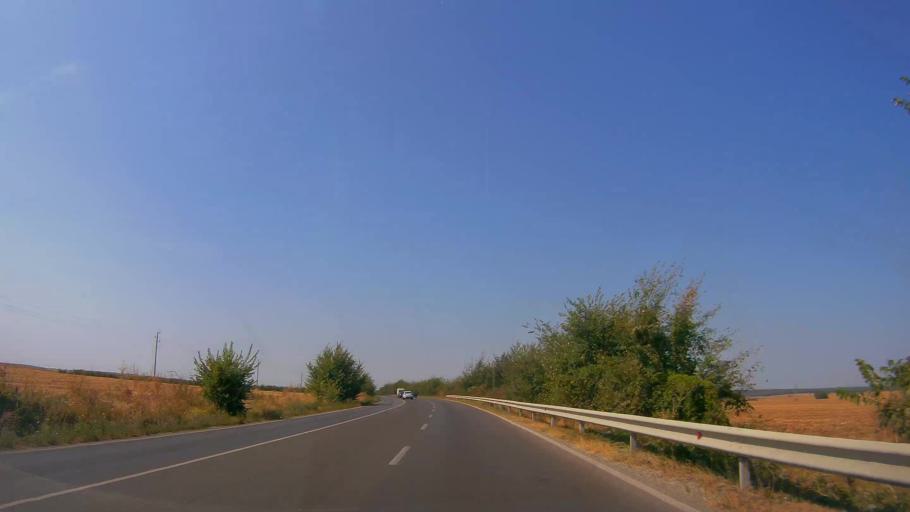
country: BG
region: Ruse
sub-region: Obshtina Vetovo
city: Senovo
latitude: 43.5638
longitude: 26.3403
